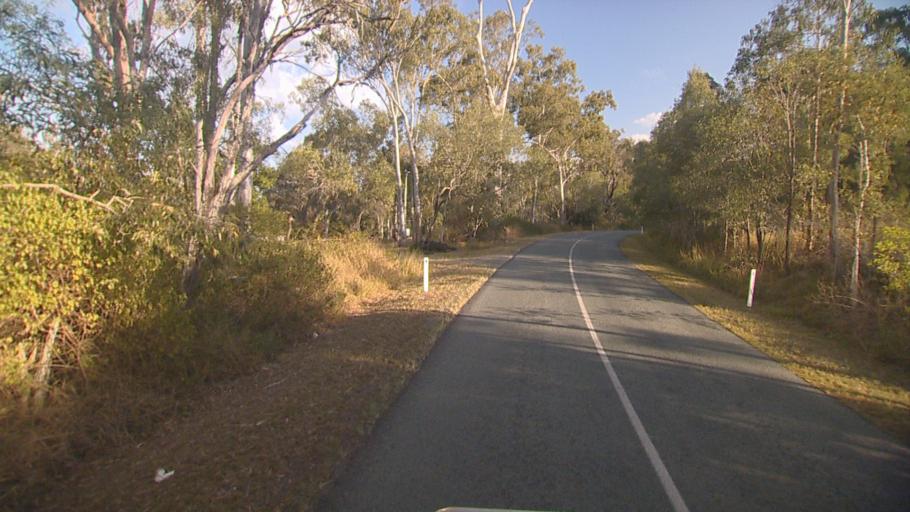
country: AU
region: Queensland
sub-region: Gold Coast
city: Ormeau Hills
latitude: -27.8370
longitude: 153.1686
